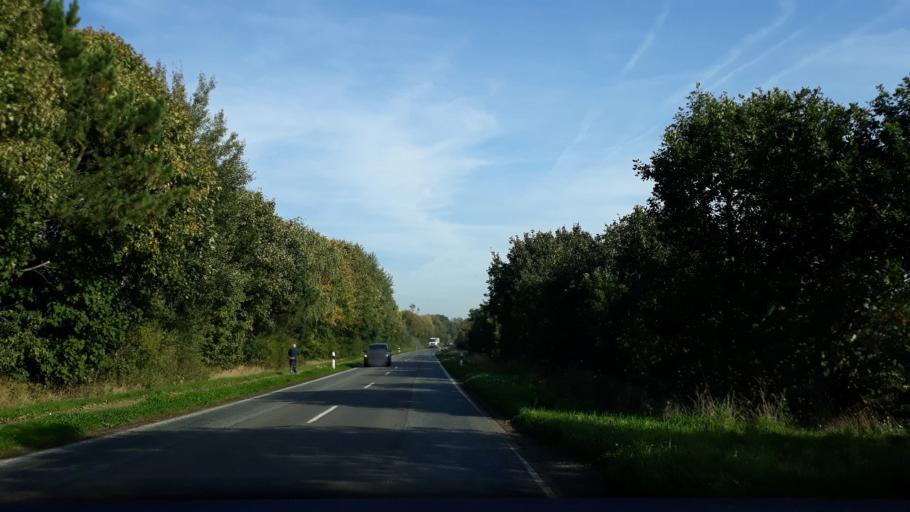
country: DE
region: Schleswig-Holstein
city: Klein Rheide
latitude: 54.4452
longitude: 9.4612
